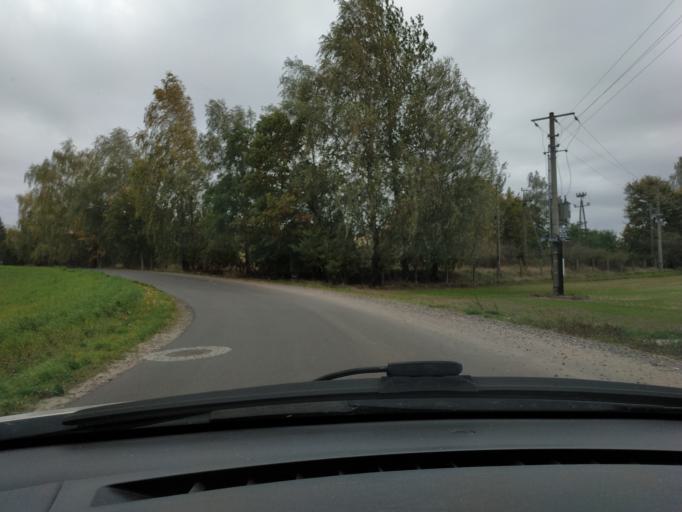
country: PL
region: Warmian-Masurian Voivodeship
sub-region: Powiat nowomiejski
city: Biskupiec
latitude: 53.4841
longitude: 19.3765
